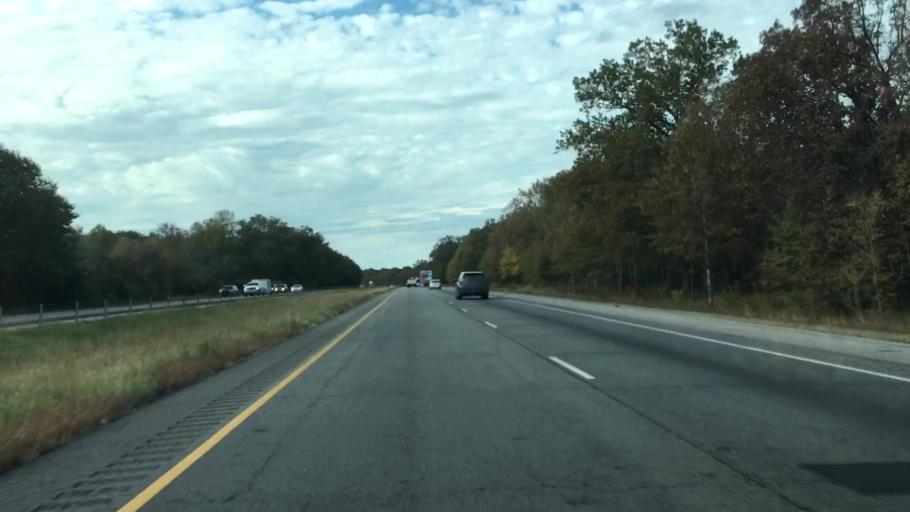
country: US
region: Arkansas
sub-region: Pope County
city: Atkins
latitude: 35.2401
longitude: -92.8578
